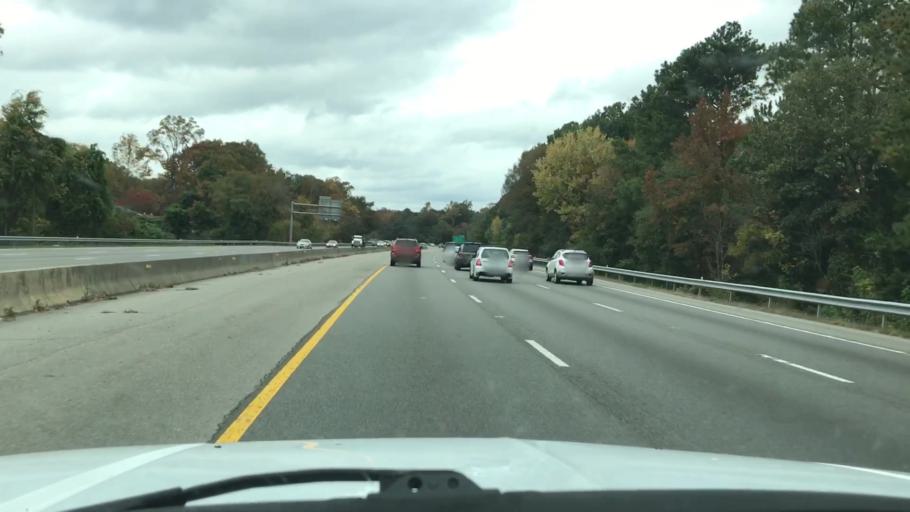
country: US
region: Virginia
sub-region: Henrico County
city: Tuckahoe
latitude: 37.6156
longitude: -77.5410
